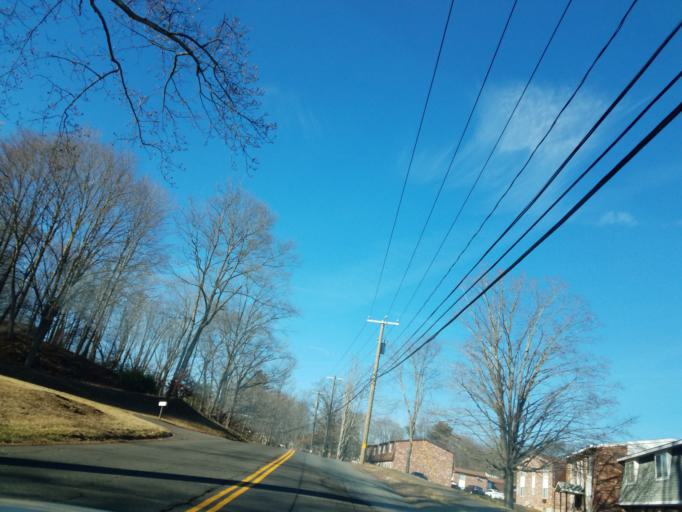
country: US
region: Connecticut
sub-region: New Haven County
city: Meriden
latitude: 41.5378
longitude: -72.8282
